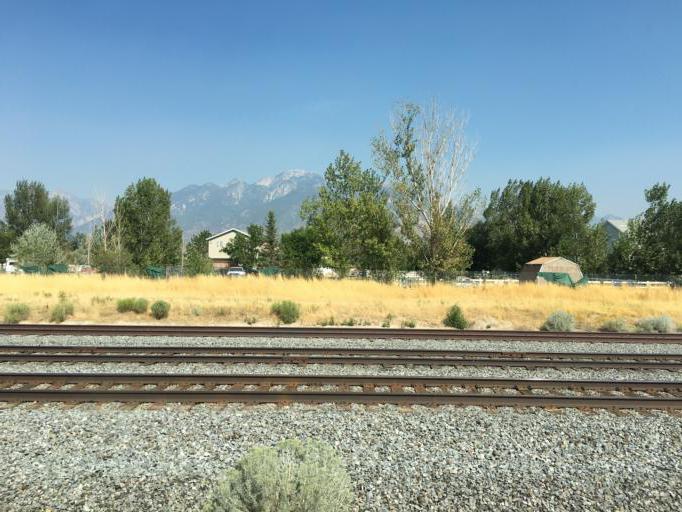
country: US
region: Utah
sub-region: Salt Lake County
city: Riverton
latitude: 40.5147
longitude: -111.9043
